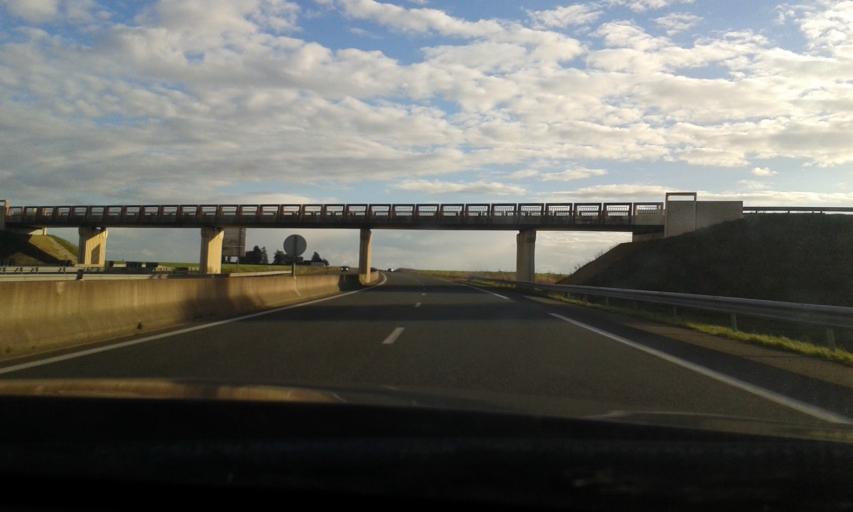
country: FR
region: Centre
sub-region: Departement d'Eure-et-Loir
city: Villemeux-sur-Eure
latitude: 48.5971
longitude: 1.4233
